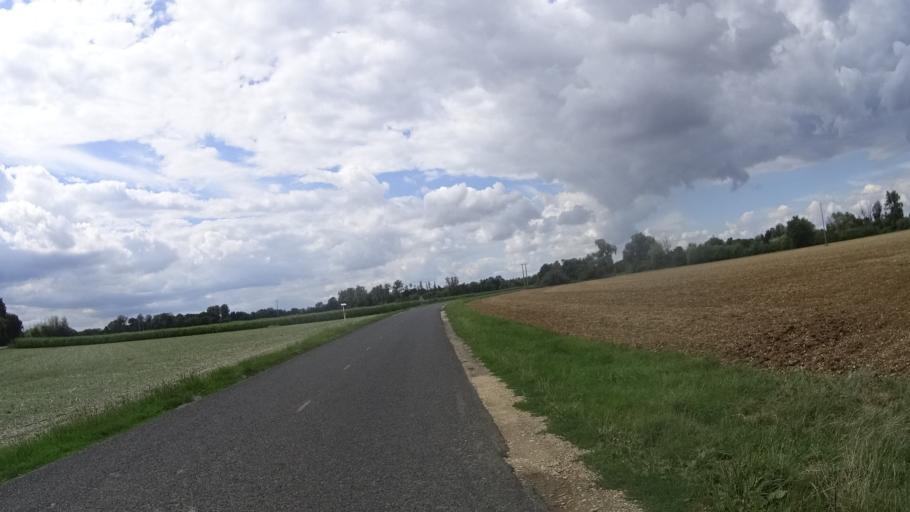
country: FR
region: Champagne-Ardenne
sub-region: Departement de la Haute-Marne
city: Villiers-en-Lieu
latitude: 48.6473
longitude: 4.8330
